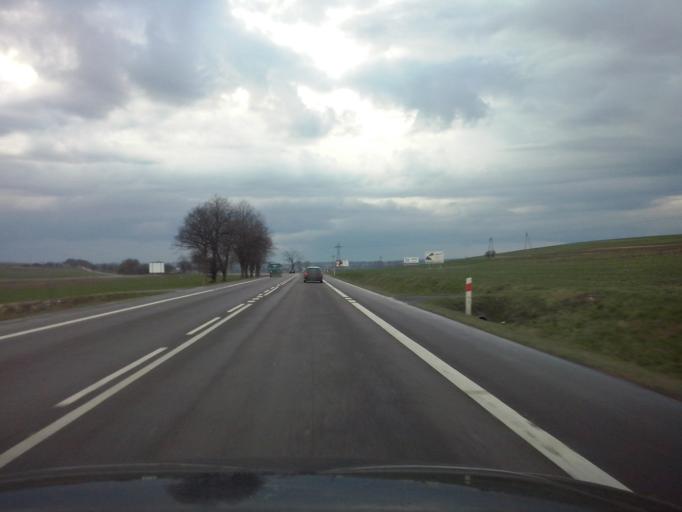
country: PL
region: Lublin Voivodeship
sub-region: Chelm
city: Chelm
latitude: 51.1644
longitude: 23.3829
